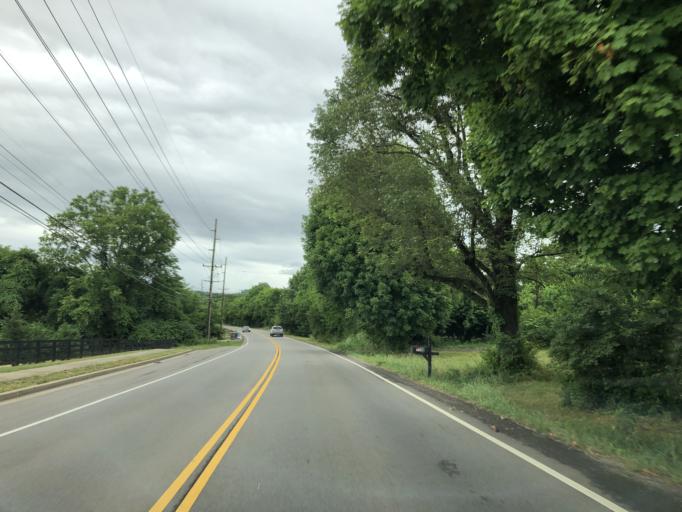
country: US
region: Tennessee
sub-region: Davidson County
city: Nashville
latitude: 36.2560
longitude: -86.7772
